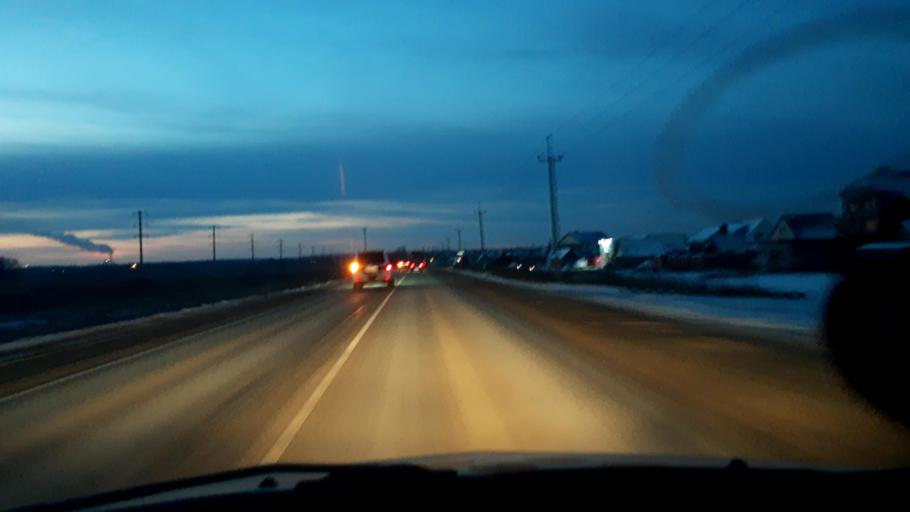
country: RU
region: Bashkortostan
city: Iglino
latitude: 54.7903
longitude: 56.2518
